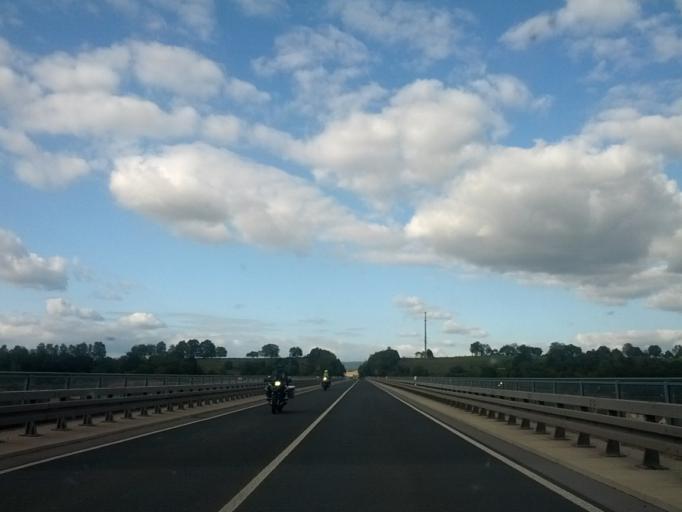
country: DE
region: Thuringia
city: Wernshausen
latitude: 50.7137
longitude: 10.3671
